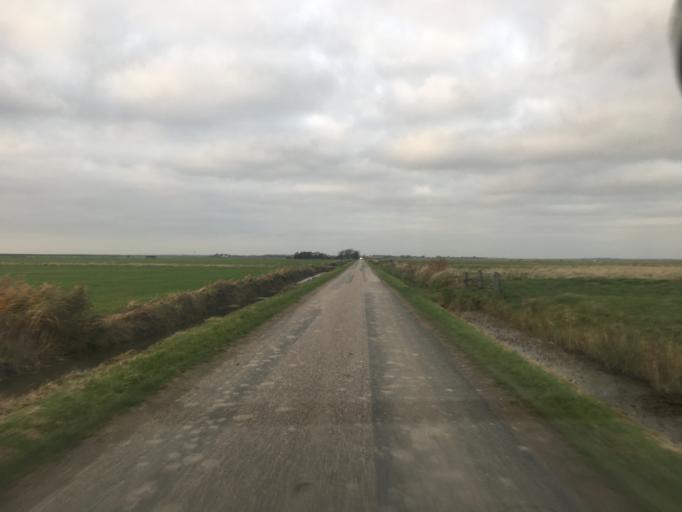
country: DE
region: Schleswig-Holstein
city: Klanxbull
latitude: 54.9316
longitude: 8.6815
